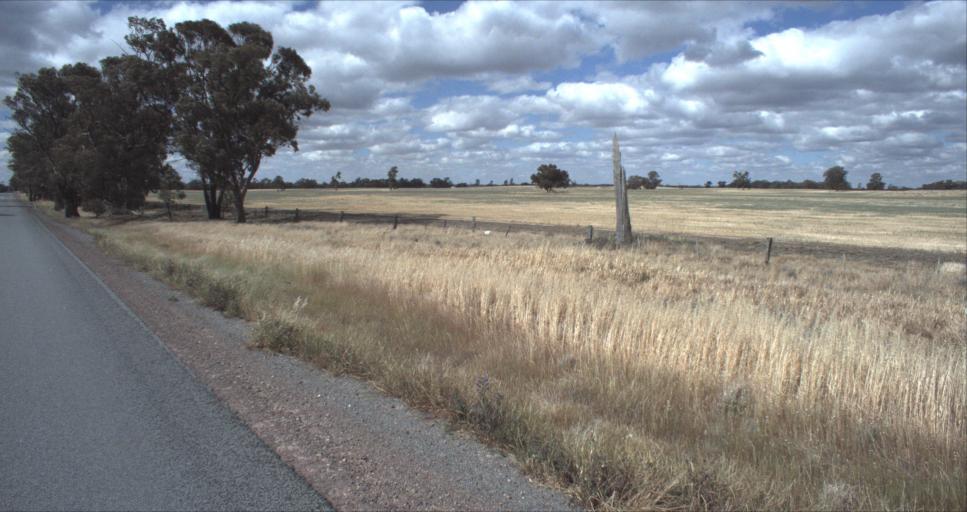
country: AU
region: New South Wales
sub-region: Leeton
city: Leeton
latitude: -34.6788
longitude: 146.3460
